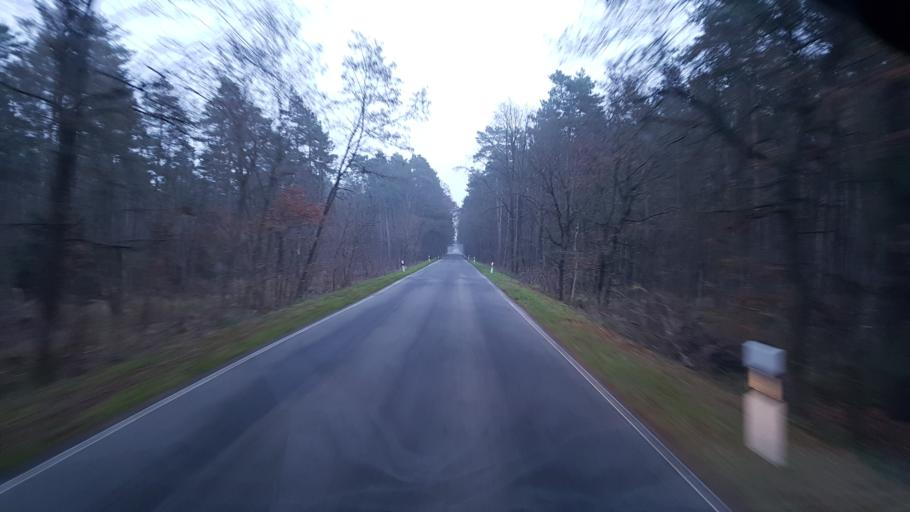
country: DE
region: Brandenburg
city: Bronkow
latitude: 51.6900
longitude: 13.9211
